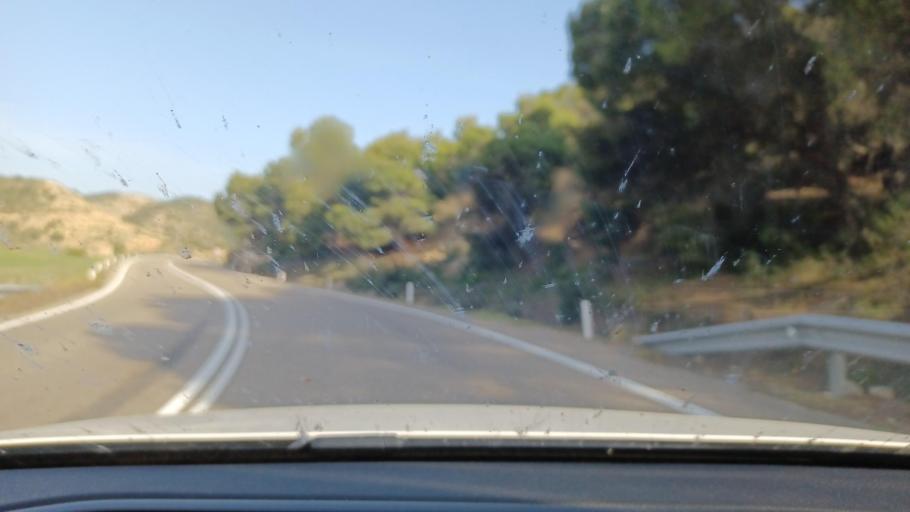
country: ES
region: Aragon
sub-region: Provincia de Zaragoza
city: Chiprana
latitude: 41.3479
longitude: -0.0917
